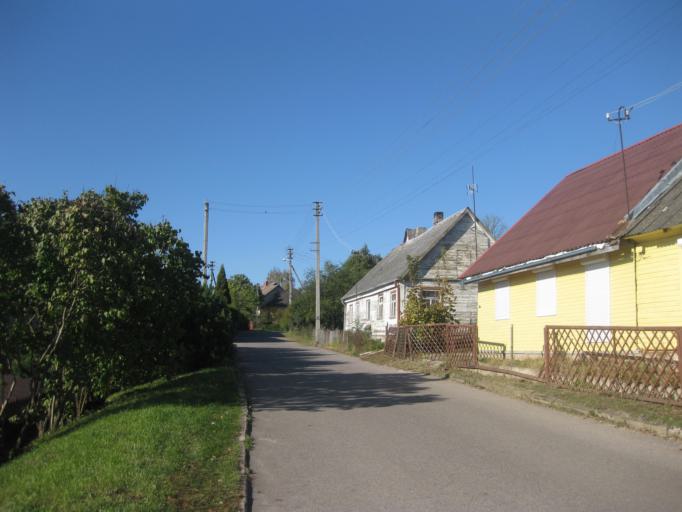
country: LT
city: Vilkija
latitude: 55.0379
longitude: 23.5816
